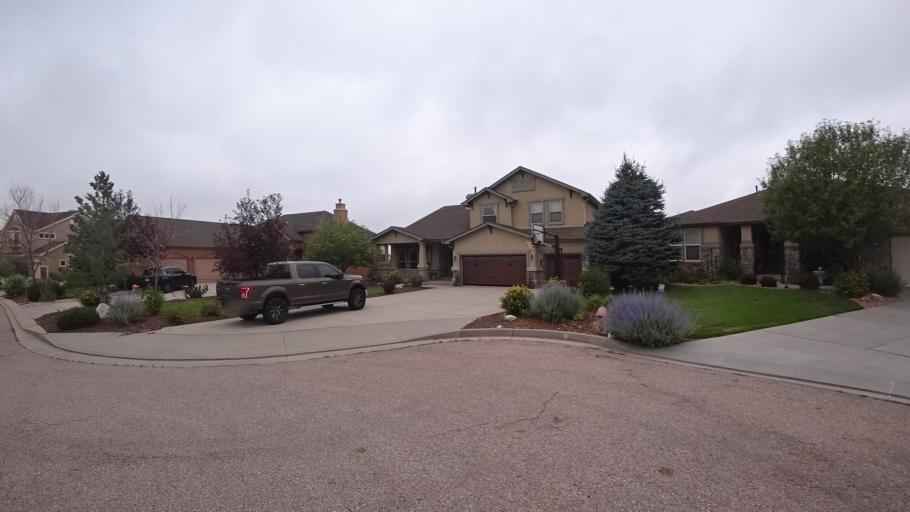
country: US
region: Colorado
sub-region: El Paso County
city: Gleneagle
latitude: 39.0318
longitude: -104.7871
